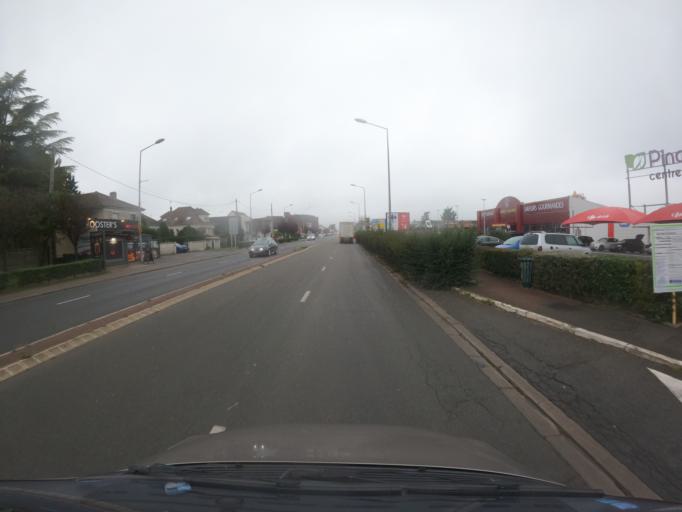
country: FR
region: Ile-de-France
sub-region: Departement du Val-de-Marne
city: Ormesson-sur-Marne
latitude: 48.7935
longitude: 2.5533
